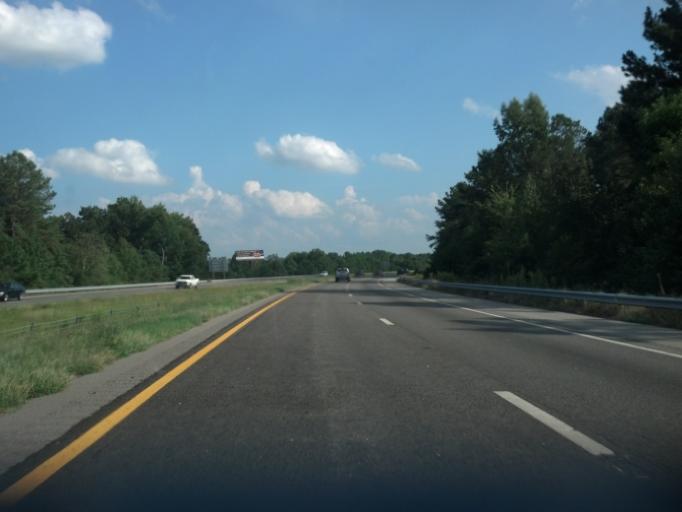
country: US
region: North Carolina
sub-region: Edgecombe County
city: Princeville
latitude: 35.8837
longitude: -77.5321
